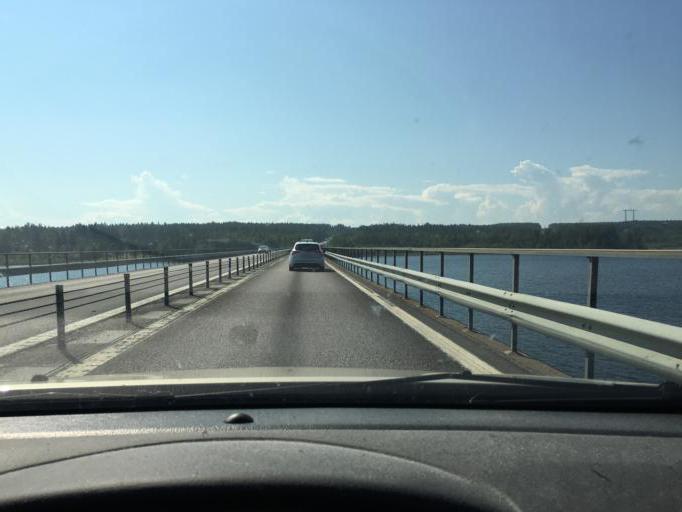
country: SE
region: Norrbotten
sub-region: Lulea Kommun
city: Gammelstad
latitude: 65.5911
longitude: 22.0300
